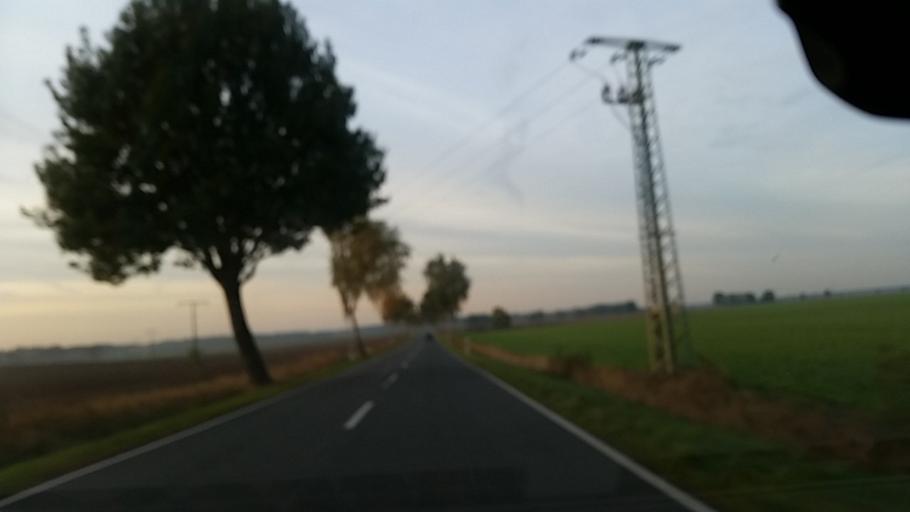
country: DE
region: Lower Saxony
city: Wittingen
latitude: 52.6900
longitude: 10.8075
